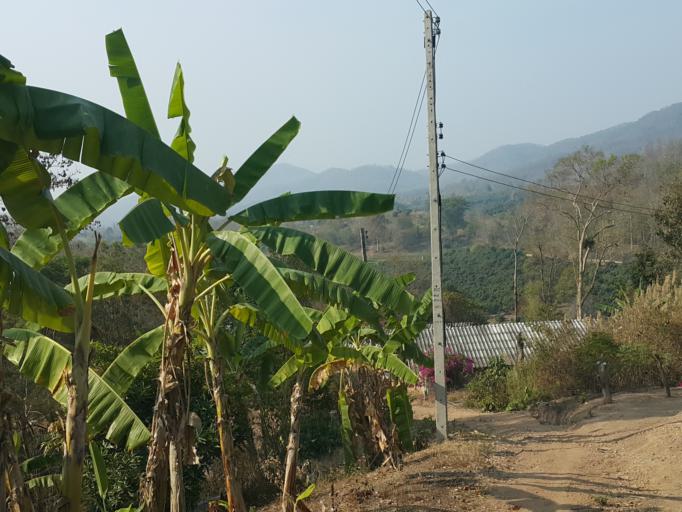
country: TH
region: Chiang Mai
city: Hang Dong
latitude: 18.7401
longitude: 98.8641
